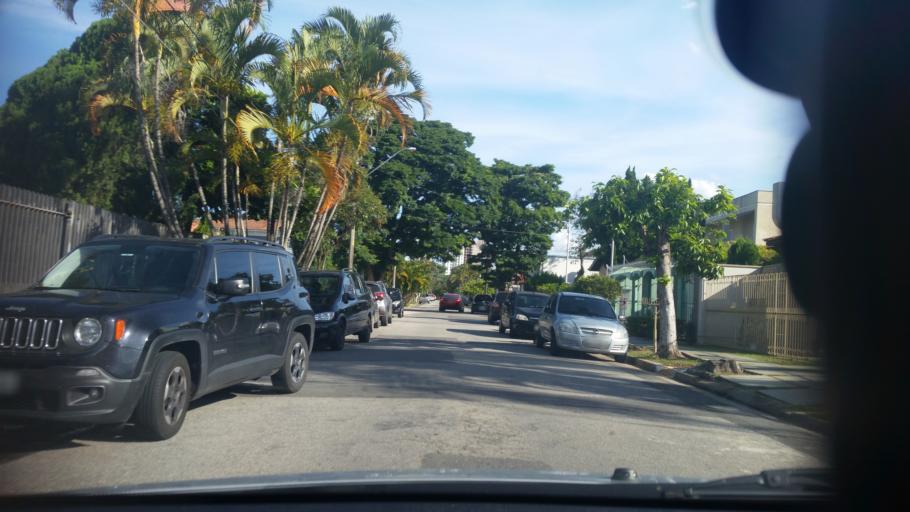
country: BR
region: Sao Paulo
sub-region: Taubate
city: Taubate
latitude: -23.0288
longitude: -45.5732
